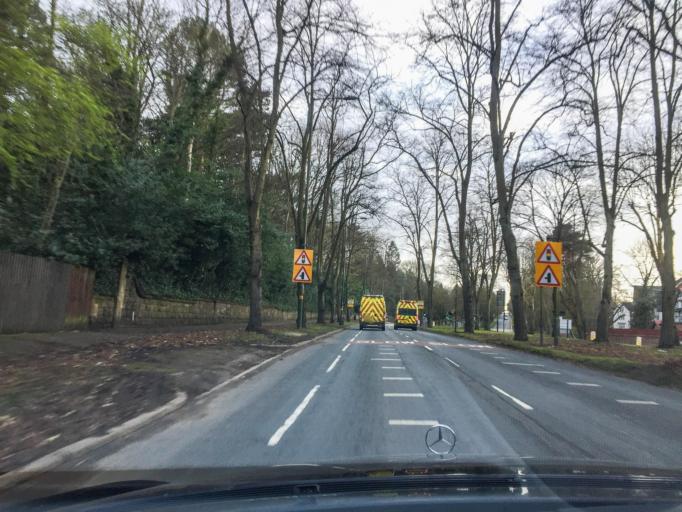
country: GB
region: England
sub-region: City and Borough of Birmingham
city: Bartley Green
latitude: 52.4251
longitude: -1.9554
